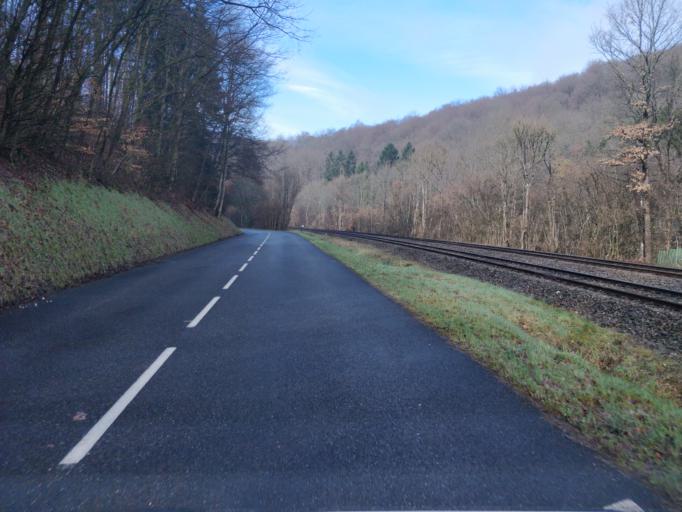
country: FR
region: Lorraine
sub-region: Departement de la Moselle
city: Soucht
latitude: 48.9233
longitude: 7.2961
